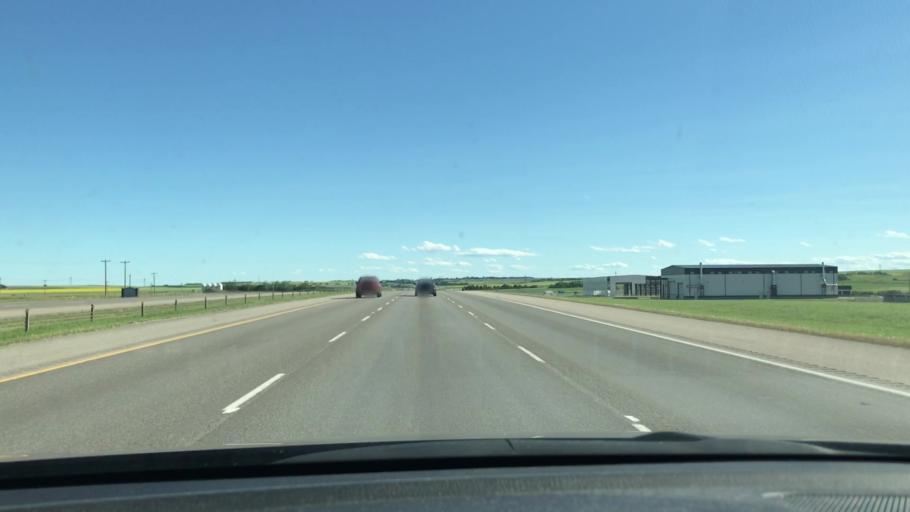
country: CA
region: Alberta
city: Crossfield
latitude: 51.4957
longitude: -114.0253
